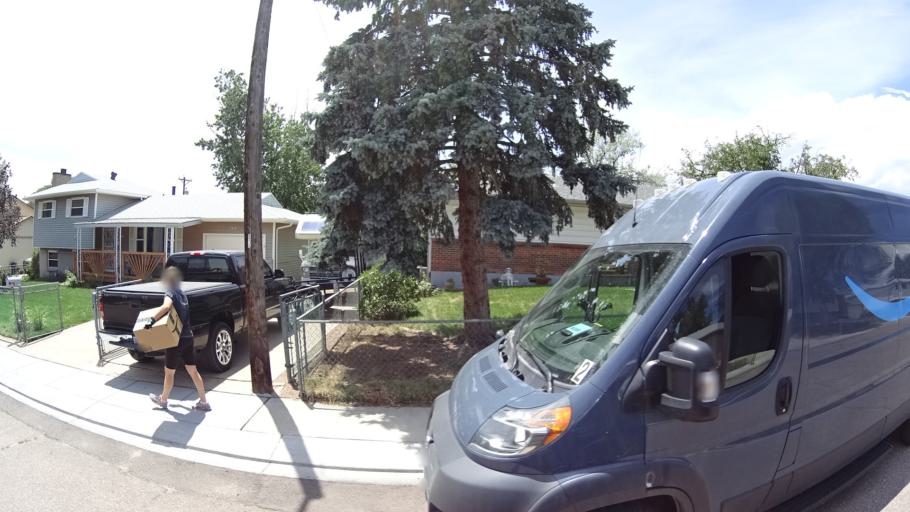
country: US
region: Colorado
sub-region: El Paso County
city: Security-Widefield
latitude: 38.7322
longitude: -104.7308
